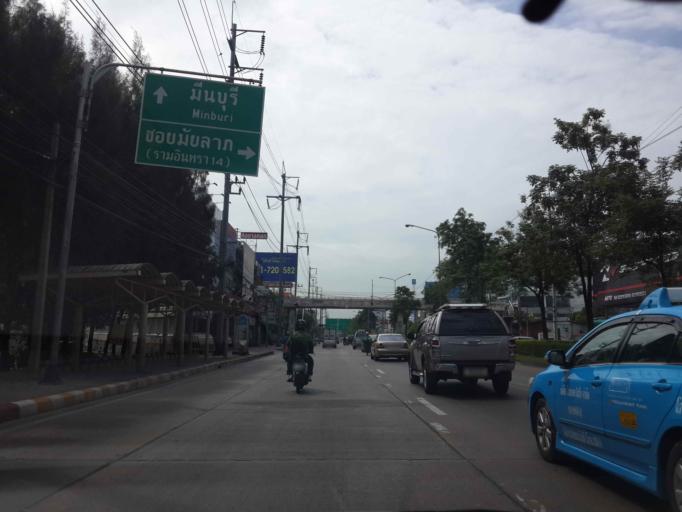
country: TH
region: Bangkok
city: Bang Khen
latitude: 13.8563
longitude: 100.6299
